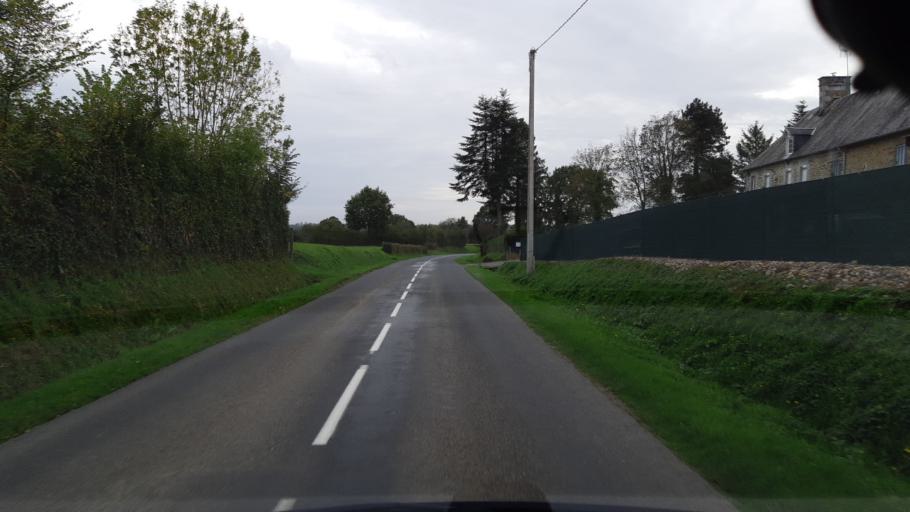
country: FR
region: Lower Normandy
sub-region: Departement de la Manche
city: Percy
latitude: 49.0101
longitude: -1.1767
